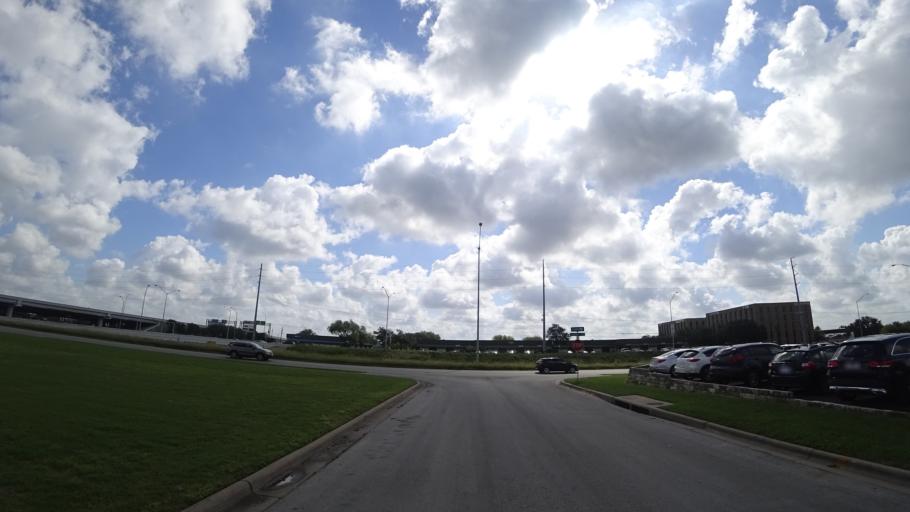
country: US
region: Texas
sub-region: Travis County
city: Austin
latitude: 30.3465
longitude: -97.7140
